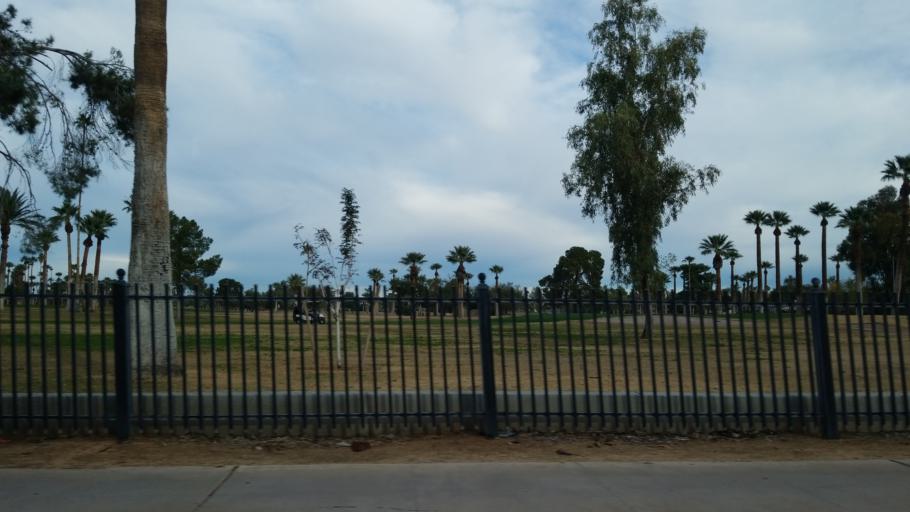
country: US
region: Arizona
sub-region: Maricopa County
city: Phoenix
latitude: 33.4728
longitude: -112.0848
